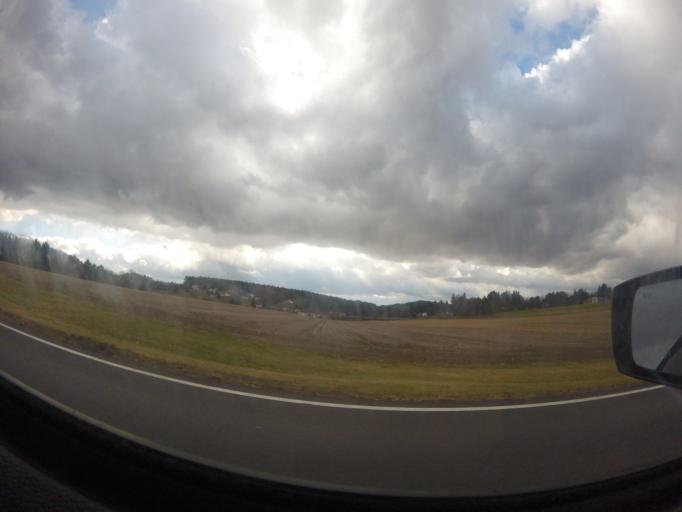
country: US
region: Maryland
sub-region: Garrett County
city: Oakland
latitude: 39.4094
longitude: -79.3945
